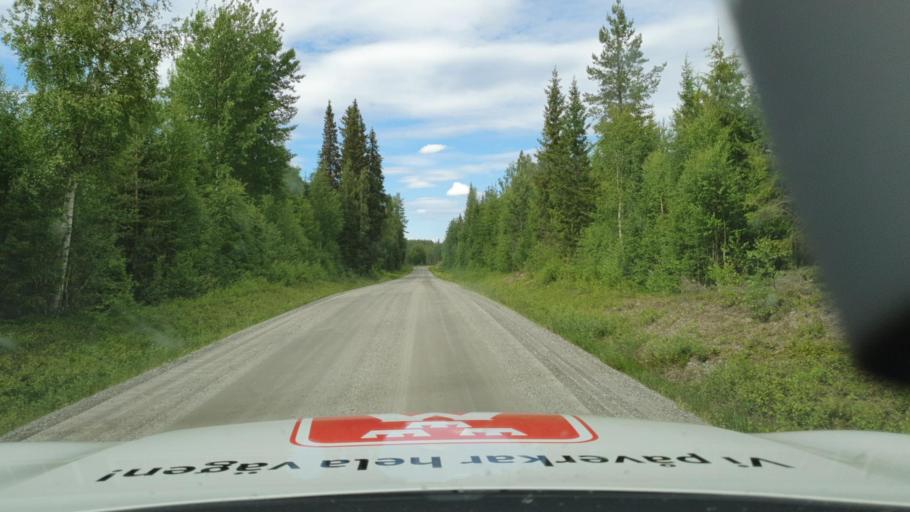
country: SE
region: Vaesterbotten
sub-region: Norsjo Kommun
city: Norsjoe
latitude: 64.8252
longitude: 19.6989
